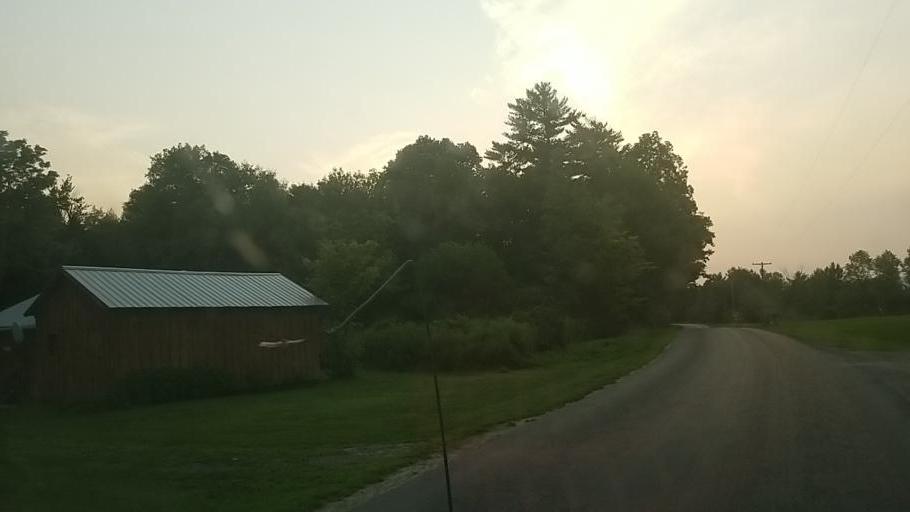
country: US
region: New York
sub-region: Montgomery County
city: Fonda
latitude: 42.9157
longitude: -74.4021
